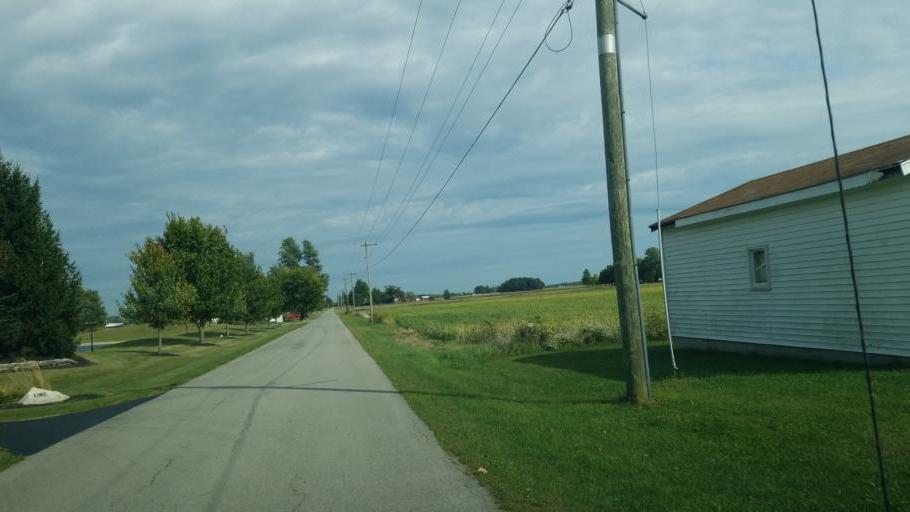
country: US
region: Ohio
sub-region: Hancock County
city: Arlington
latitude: 40.8773
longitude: -83.6215
